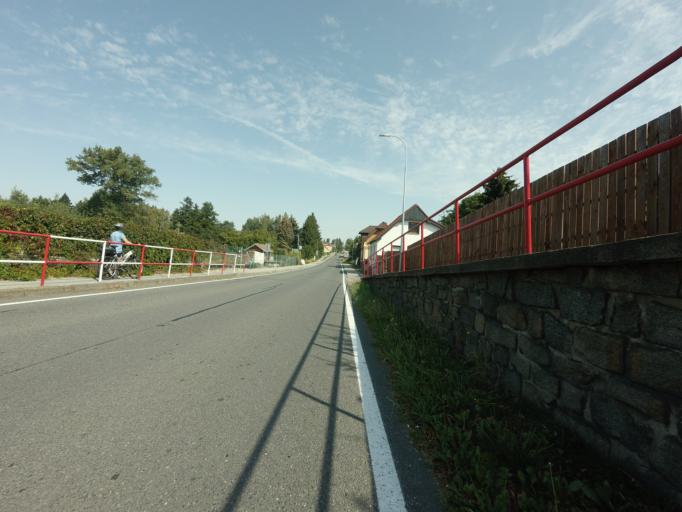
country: CZ
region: Jihocesky
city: Bernartice
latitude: 49.3697
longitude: 14.3796
